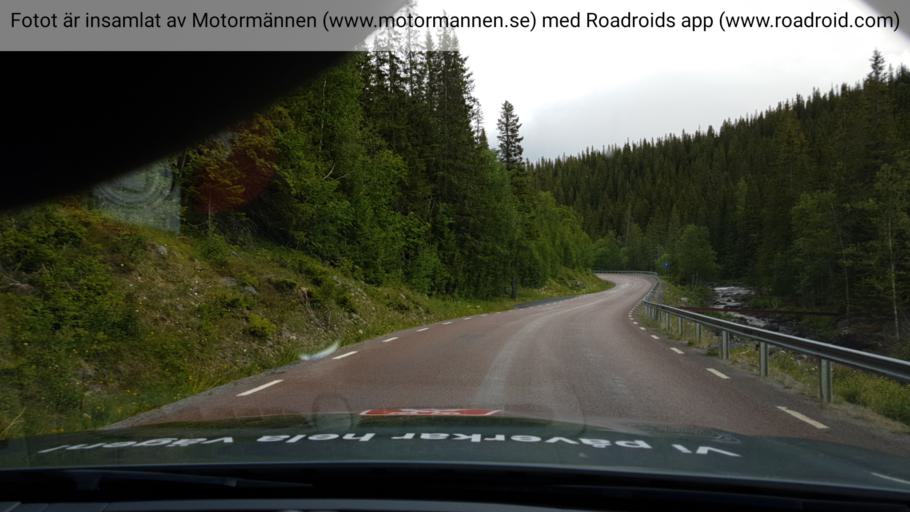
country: SE
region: Jaemtland
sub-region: Are Kommun
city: Jarpen
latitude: 63.1047
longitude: 13.8395
